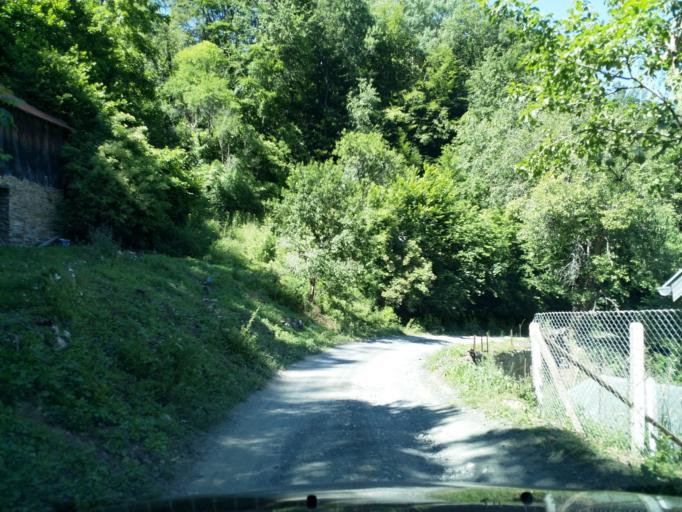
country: XK
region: Mitrovica
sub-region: Komuna e Leposaviqit
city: Leposaviq
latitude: 43.2655
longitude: 20.8682
